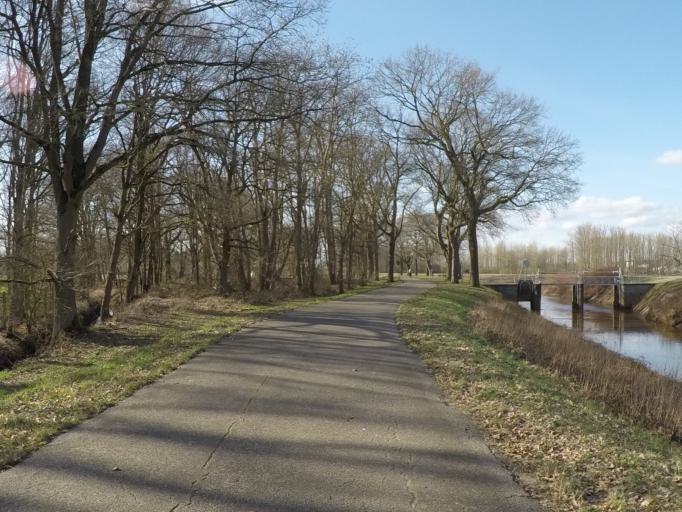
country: BE
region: Flanders
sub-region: Provincie Antwerpen
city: Grobbendonk
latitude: 51.1772
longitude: 4.7135
